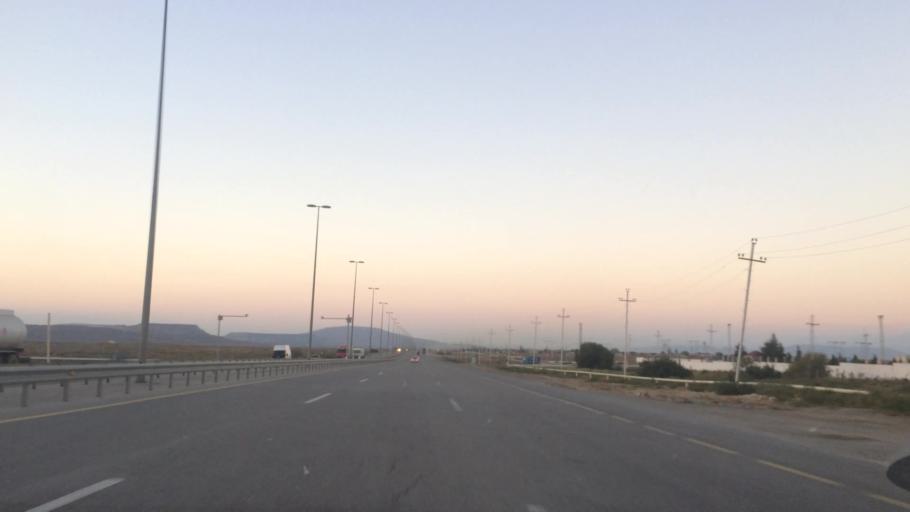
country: AZ
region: Baki
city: Qobustan
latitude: 40.0014
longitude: 49.4299
